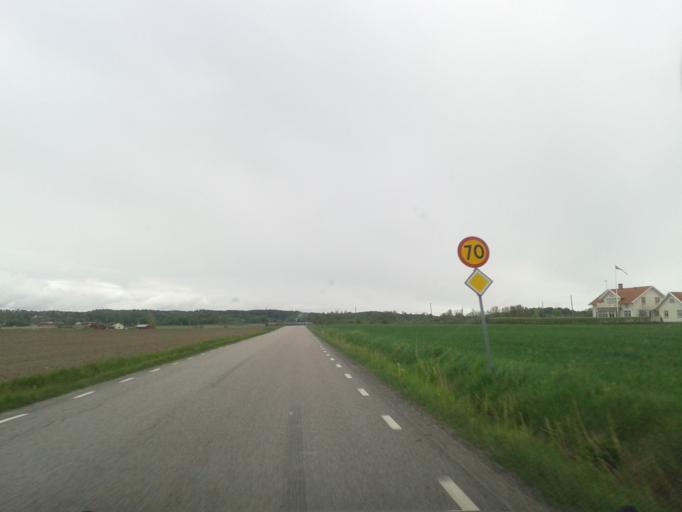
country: SE
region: Vaestra Goetaland
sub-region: Kungalvs Kommun
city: Kode
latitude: 57.9397
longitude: 11.8214
